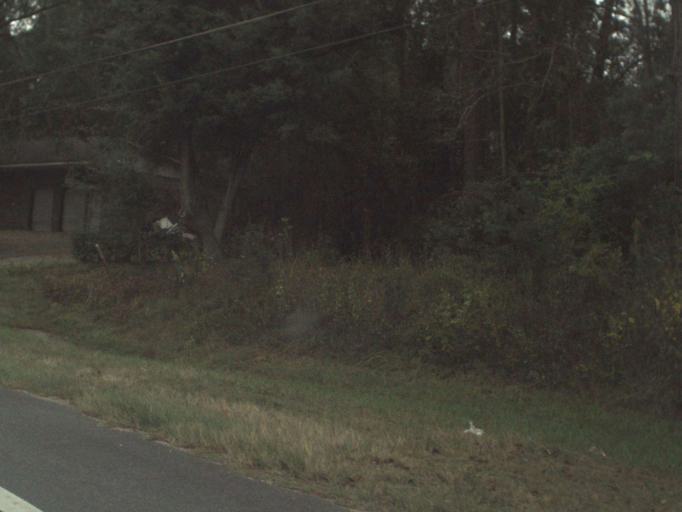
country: US
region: Florida
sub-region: Gadsden County
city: Midway
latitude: 30.5099
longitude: -84.3623
